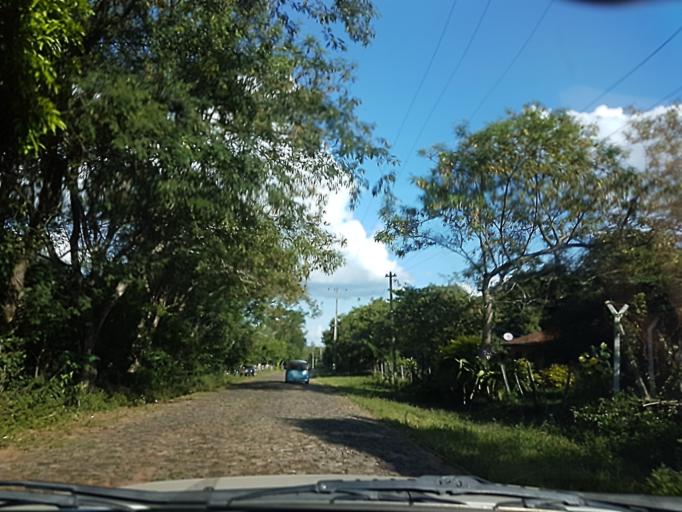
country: PY
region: Cordillera
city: Arroyos y Esteros
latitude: -25.0042
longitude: -57.1355
